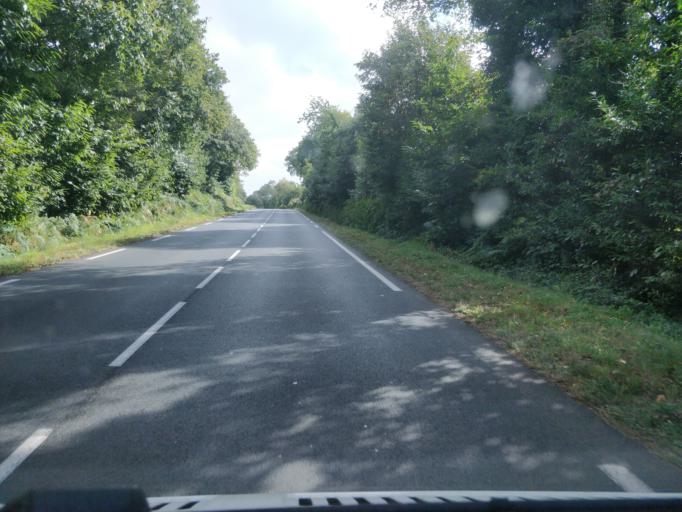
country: FR
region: Brittany
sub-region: Departement du Finistere
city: Plogastel-Saint-Germain
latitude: 47.9978
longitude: -4.2889
